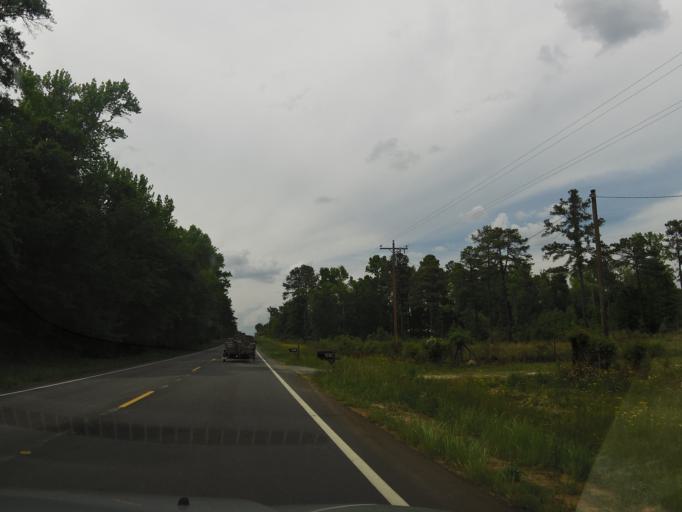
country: US
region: Georgia
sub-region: McDuffie County
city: Thomson
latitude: 33.3992
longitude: -82.4772
